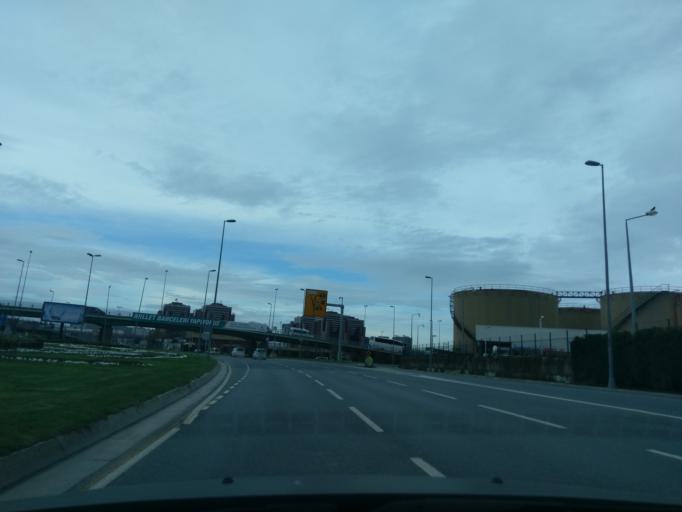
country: TR
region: Istanbul
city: Bahcelievler
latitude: 40.9821
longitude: 28.8394
